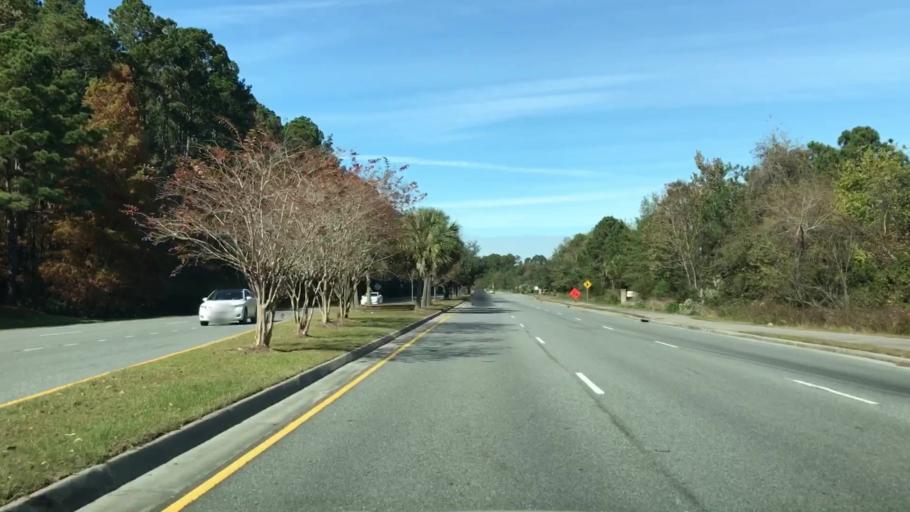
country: US
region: South Carolina
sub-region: Beaufort County
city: Bluffton
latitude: 32.2582
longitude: -80.9033
